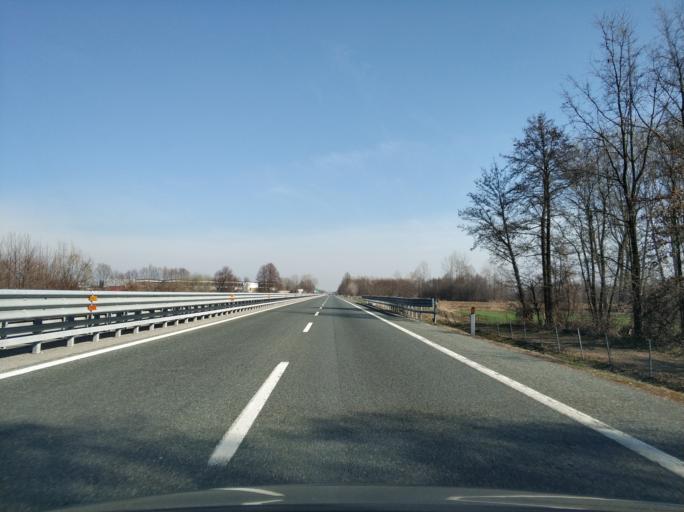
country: IT
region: Piedmont
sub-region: Provincia di Torino
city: Settimo Torinese
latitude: 45.1673
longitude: 7.7603
